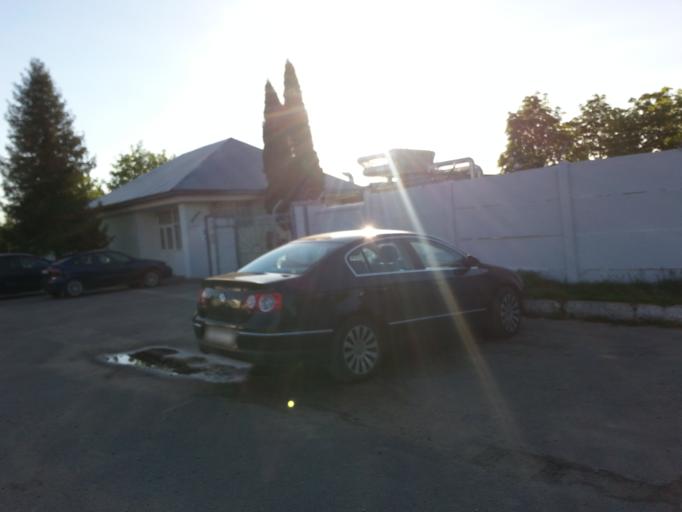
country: BY
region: Minsk
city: Narach
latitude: 54.9343
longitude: 26.6768
